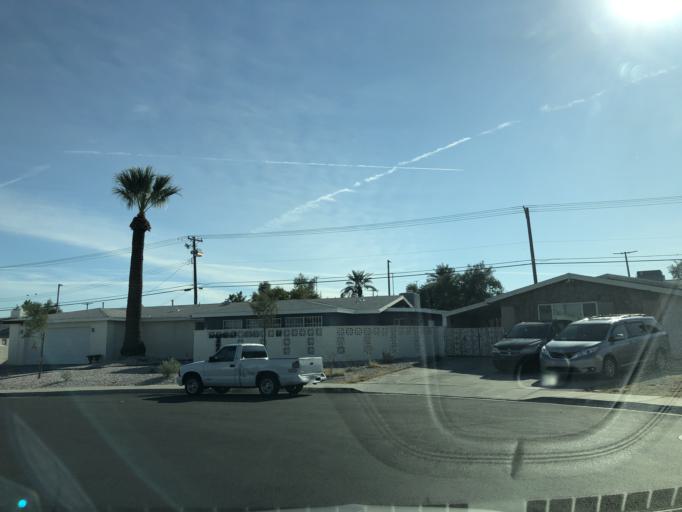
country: US
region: Nevada
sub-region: Clark County
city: Winchester
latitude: 36.1265
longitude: -115.1342
